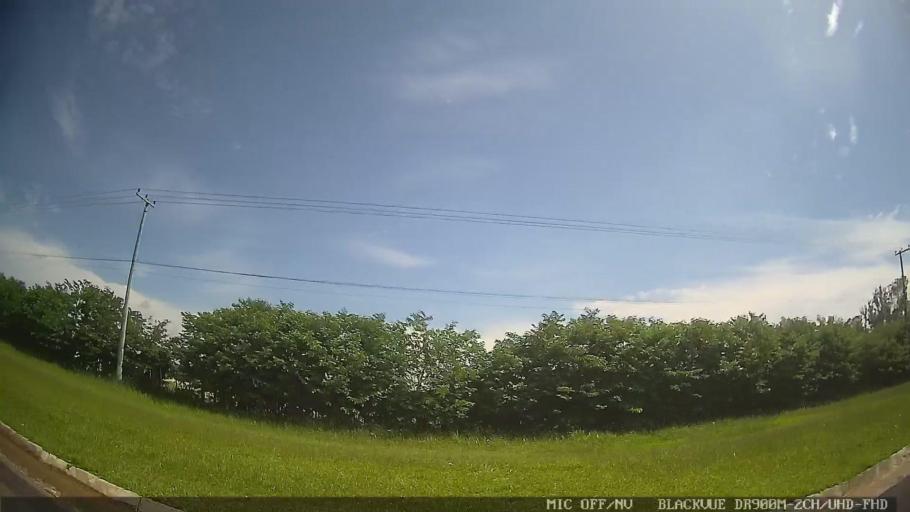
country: BR
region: Sao Paulo
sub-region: Porto Feliz
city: Porto Feliz
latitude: -23.2281
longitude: -47.5406
